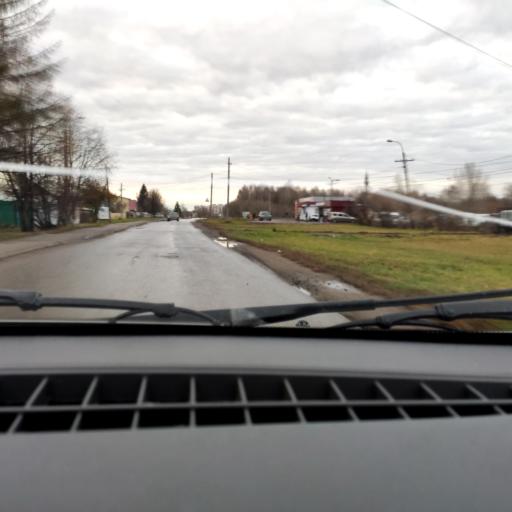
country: RU
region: Bashkortostan
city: Avdon
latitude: 54.7051
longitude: 55.8174
